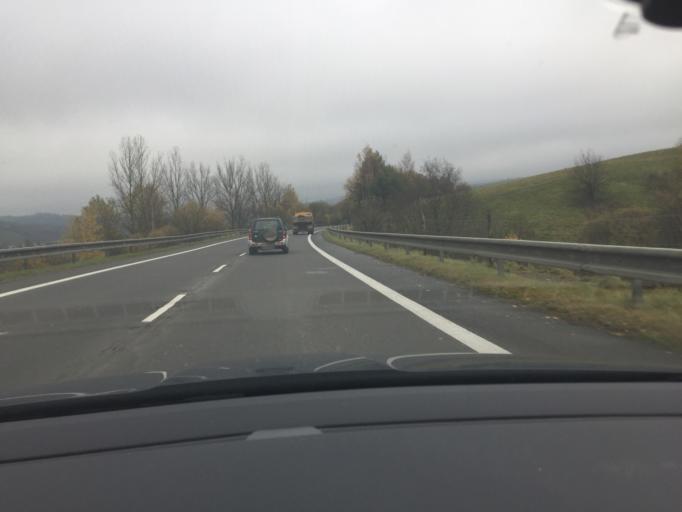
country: SK
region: Presovsky
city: Stara L'ubovna
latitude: 49.2964
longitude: 20.7163
